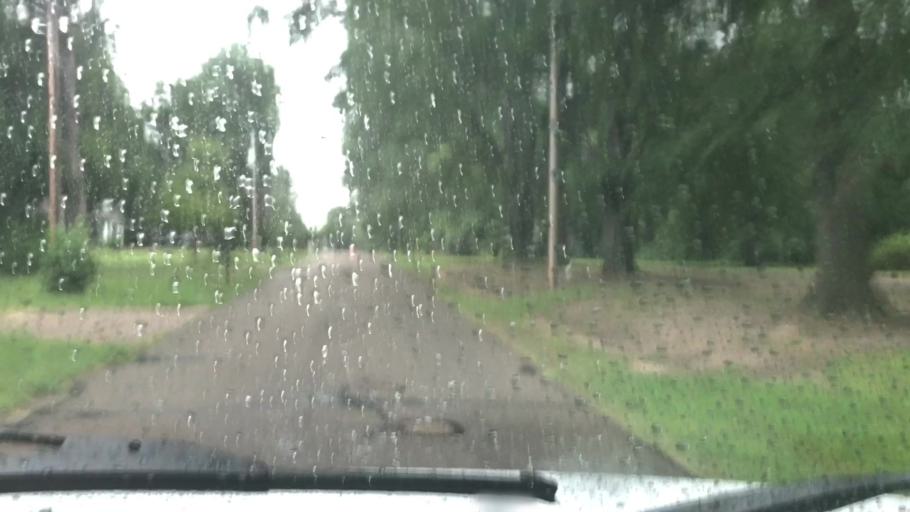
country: US
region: Texas
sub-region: Bowie County
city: Wake Village
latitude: 33.3954
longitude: -94.0856
